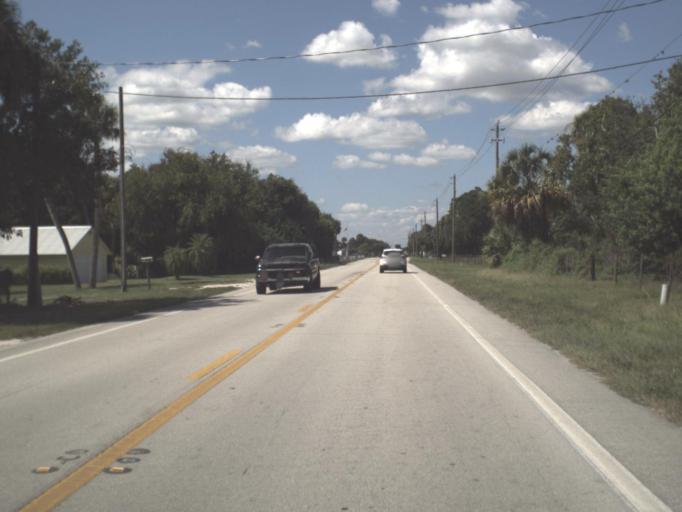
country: US
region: Florida
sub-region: Okeechobee County
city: Taylor Creek
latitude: 27.1898
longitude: -80.7513
